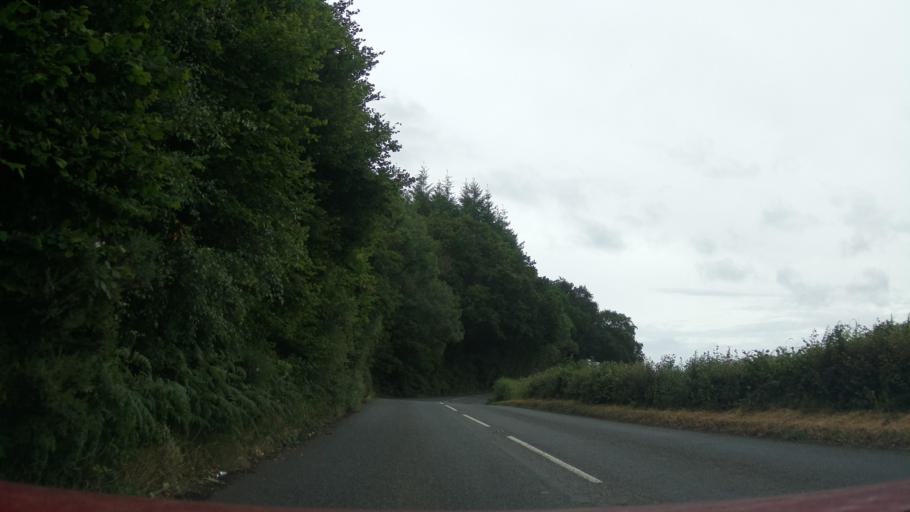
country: GB
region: England
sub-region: Devon
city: Chudleigh
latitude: 50.6037
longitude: -3.6200
